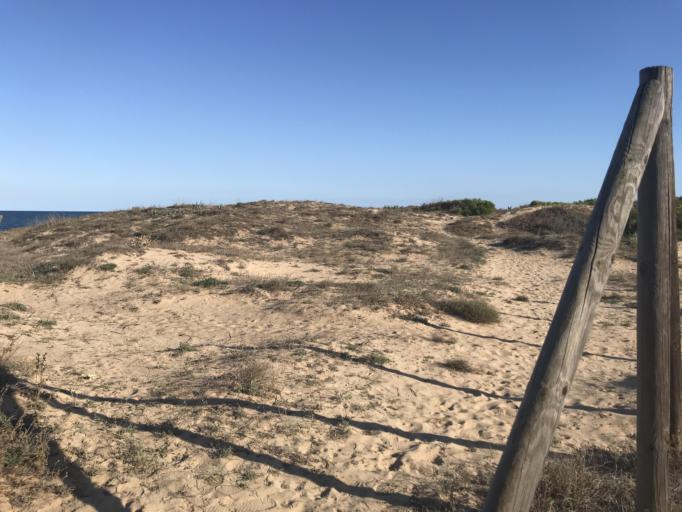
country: ES
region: Valencia
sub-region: Provincia de Alicante
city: Guardamar del Segura
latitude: 38.0313
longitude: -0.6518
